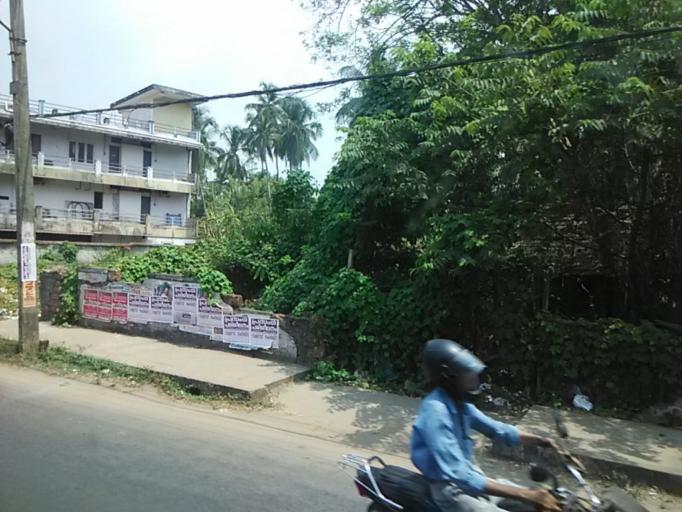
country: IN
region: Kerala
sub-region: Kozhikode
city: Kozhikode
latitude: 11.2722
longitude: 75.7754
